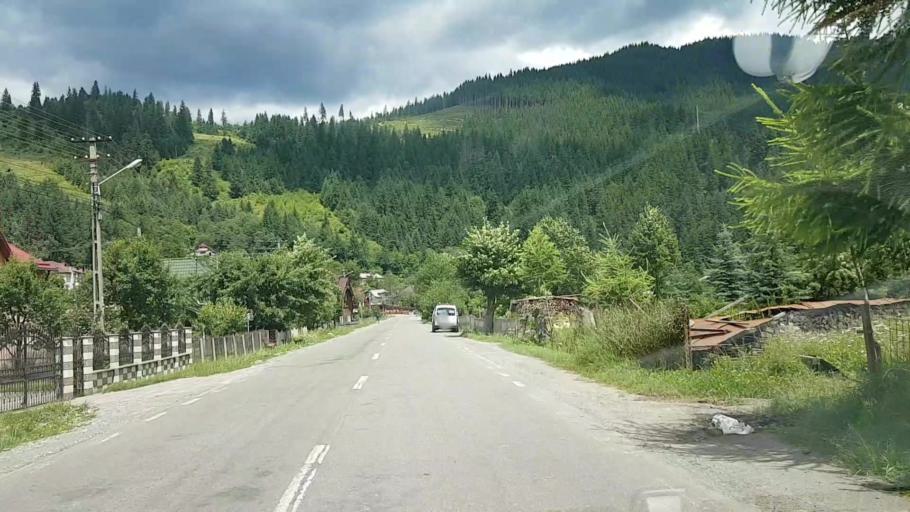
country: RO
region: Suceava
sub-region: Comuna Brosteni
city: Brosteni
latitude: 47.2409
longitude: 25.7005
